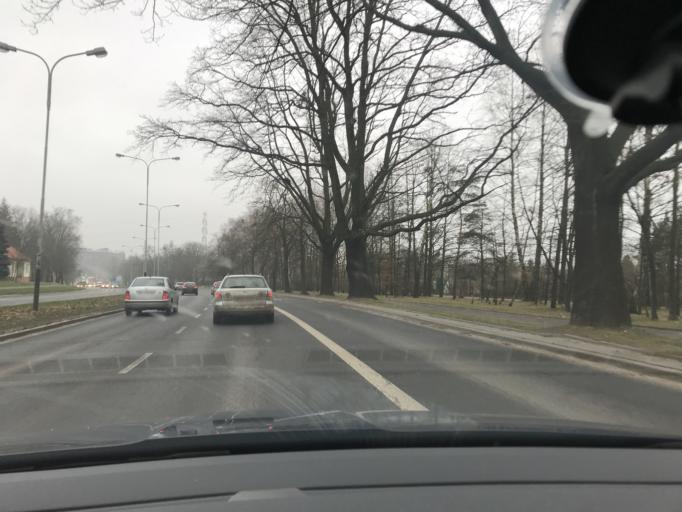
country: PL
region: Lodz Voivodeship
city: Lodz
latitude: 51.7869
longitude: 19.4837
